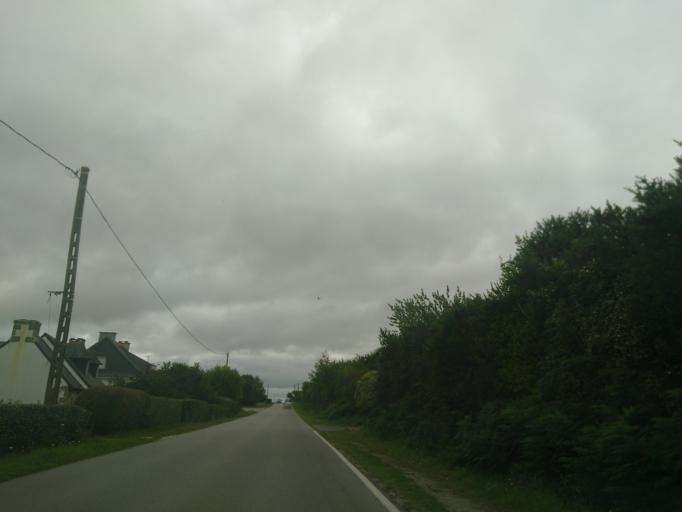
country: FR
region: Brittany
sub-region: Departement du Finistere
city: Plomodiern
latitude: 48.1682
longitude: -4.2733
